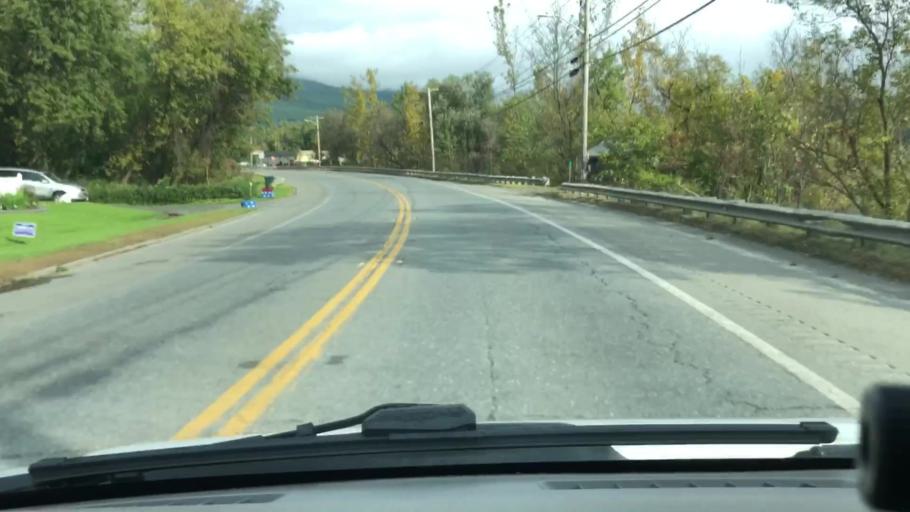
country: US
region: Massachusetts
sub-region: Berkshire County
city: North Adams
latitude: 42.6833
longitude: -73.1067
